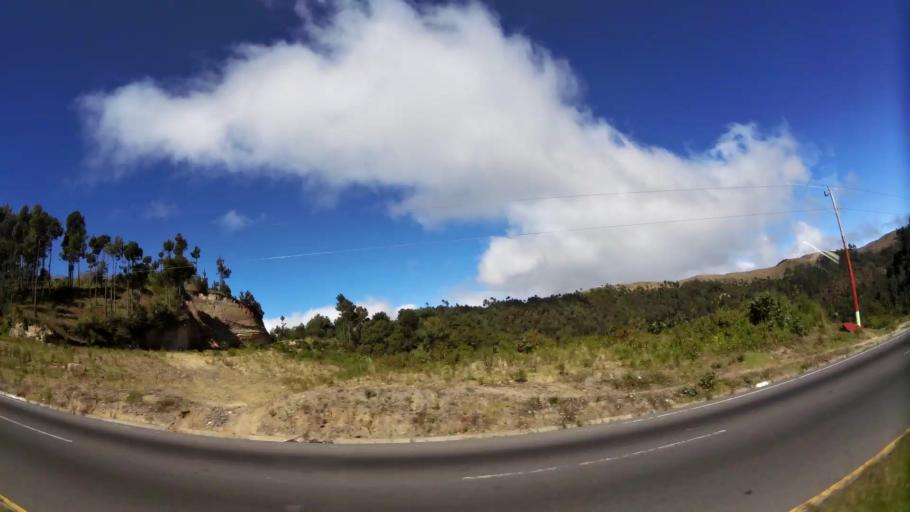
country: GT
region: Solola
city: Santa Catarina Ixtahuacan
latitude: 14.8296
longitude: -91.3567
